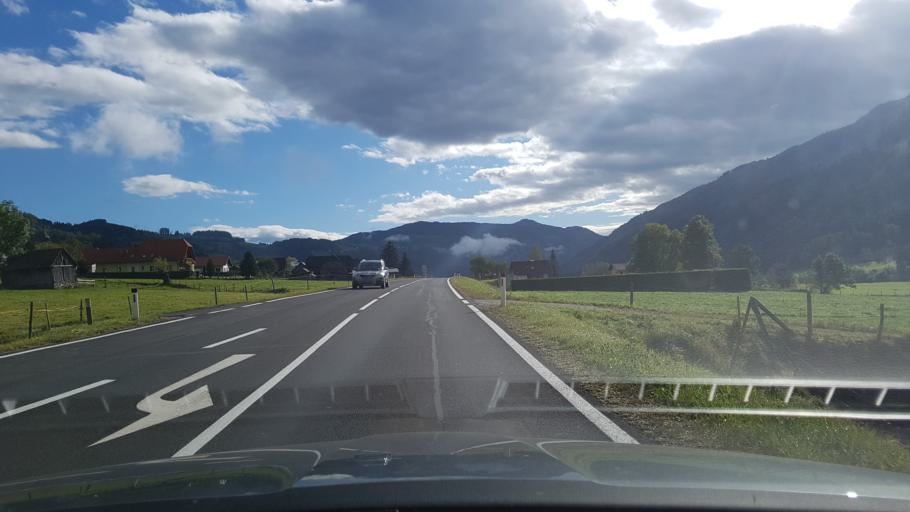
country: AT
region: Styria
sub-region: Politischer Bezirk Murau
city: Sankt Peter am Kammersberg
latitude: 47.1880
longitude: 14.1581
